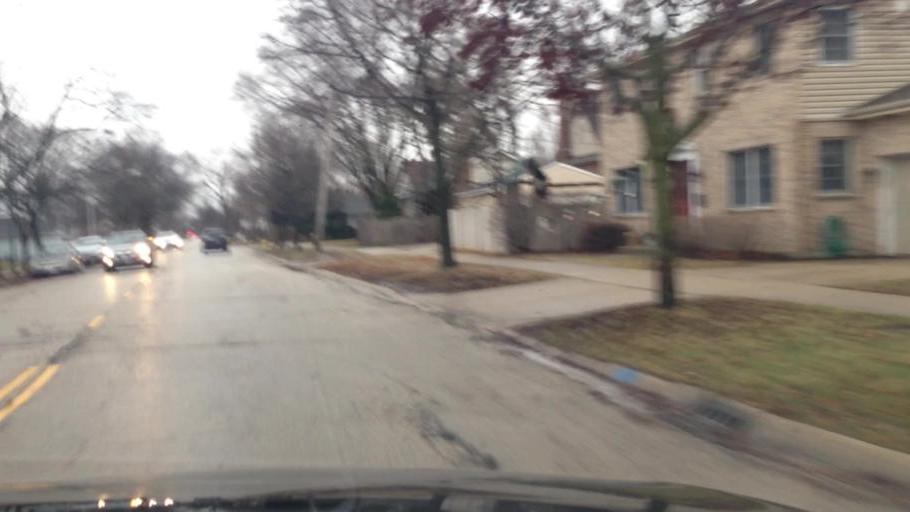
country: US
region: Illinois
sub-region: Cook County
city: Park Ridge
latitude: 42.0040
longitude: -87.8211
